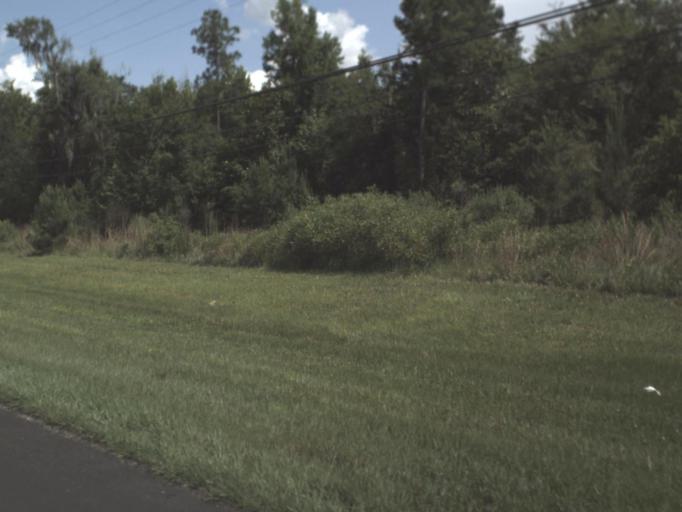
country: US
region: Florida
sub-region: Alachua County
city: Alachua
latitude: 29.7651
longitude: -82.4099
